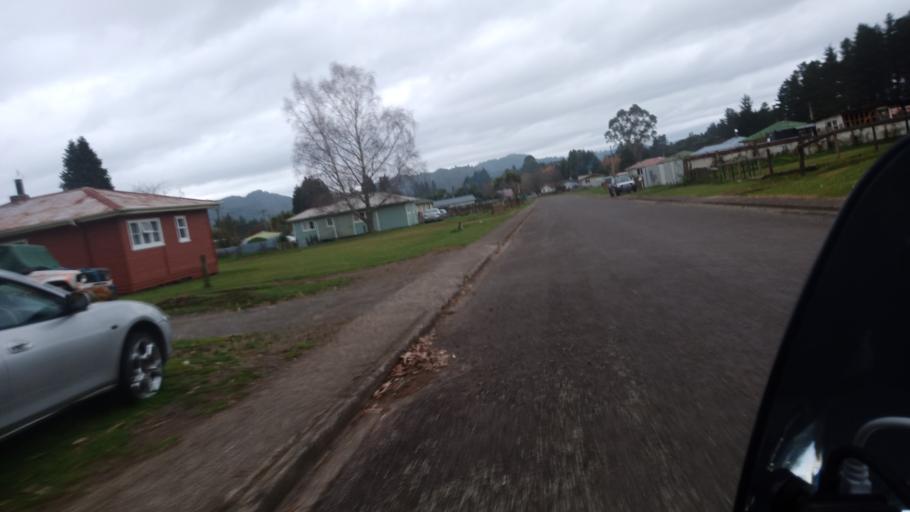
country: NZ
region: Bay of Plenty
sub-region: Whakatane District
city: Murupara
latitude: -38.6451
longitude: 176.7330
